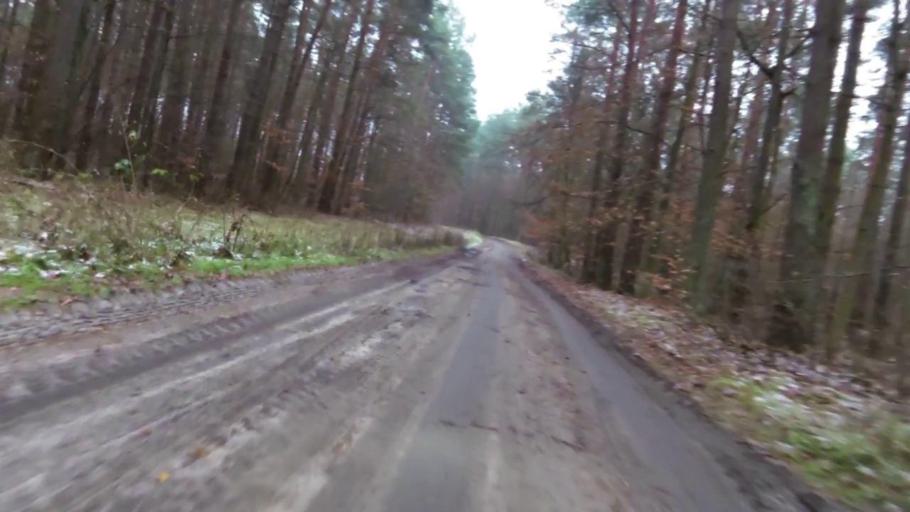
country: PL
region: West Pomeranian Voivodeship
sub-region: Powiat walecki
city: Walcz
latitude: 53.3049
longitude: 16.4703
